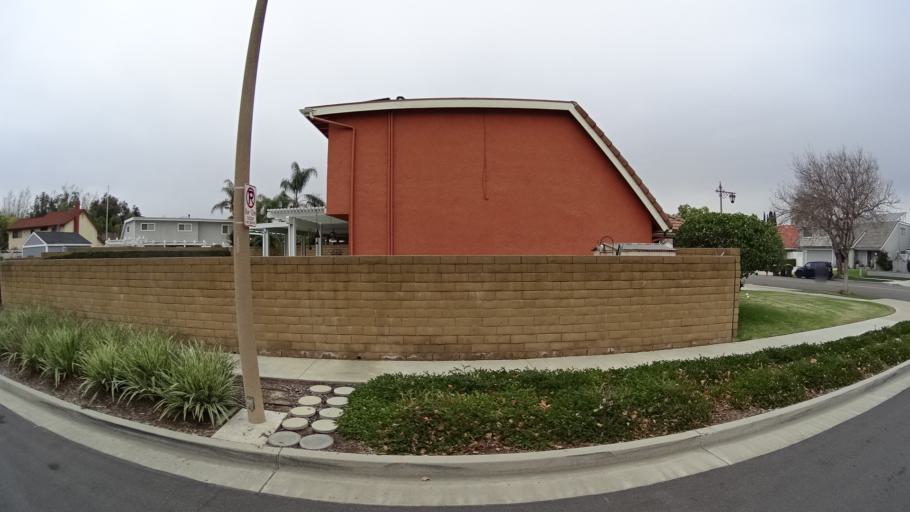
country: US
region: California
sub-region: Orange County
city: Yorba Linda
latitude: 33.8571
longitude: -117.7747
